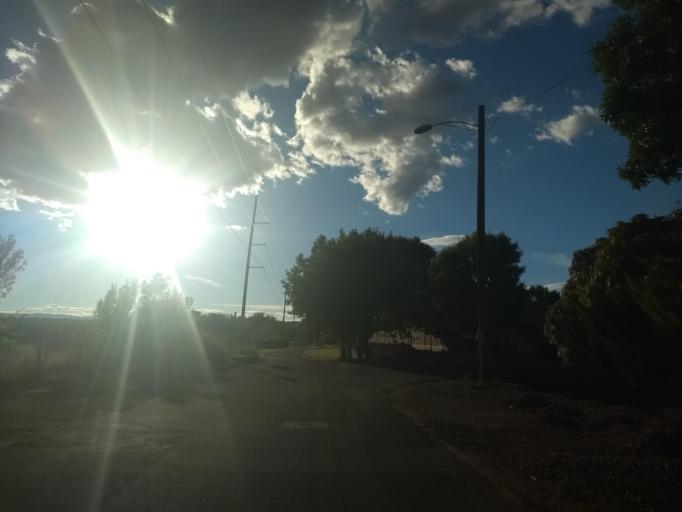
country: US
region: Utah
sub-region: Washington County
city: Washington
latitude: 37.1251
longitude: -113.5096
